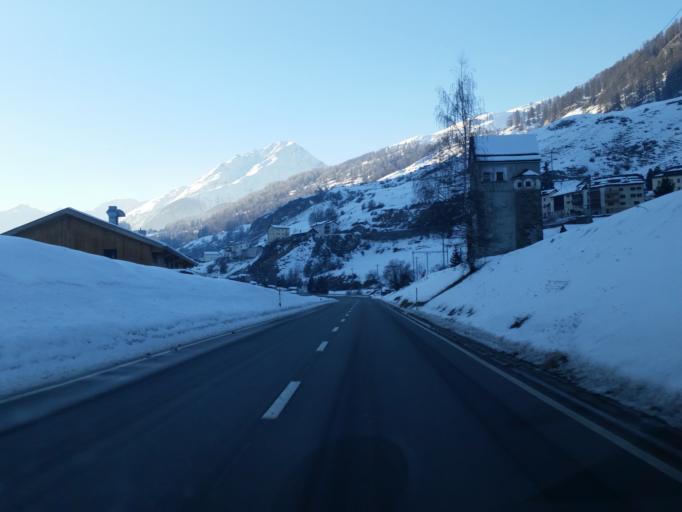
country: CH
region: Grisons
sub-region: Inn District
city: Scuol
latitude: 46.7732
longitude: 10.2013
